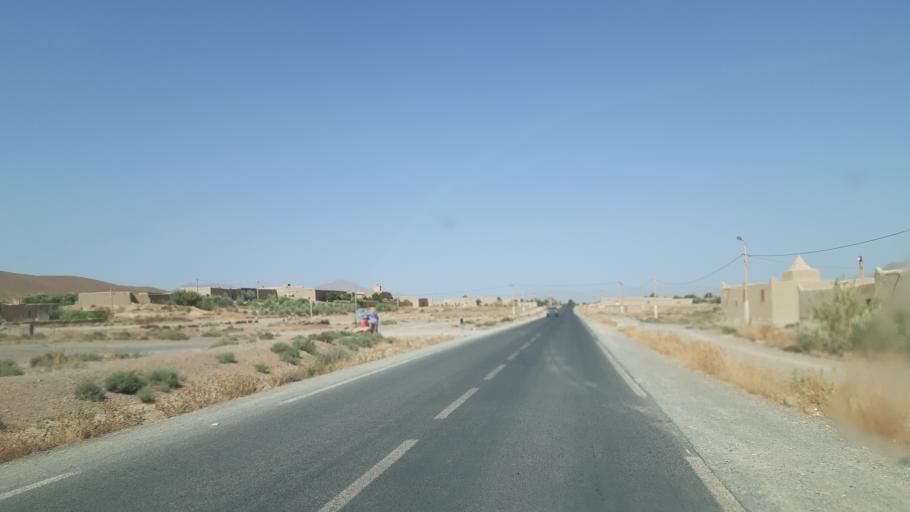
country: MA
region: Meknes-Tafilalet
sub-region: Errachidia
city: Errachidia
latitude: 32.2526
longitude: -4.5719
